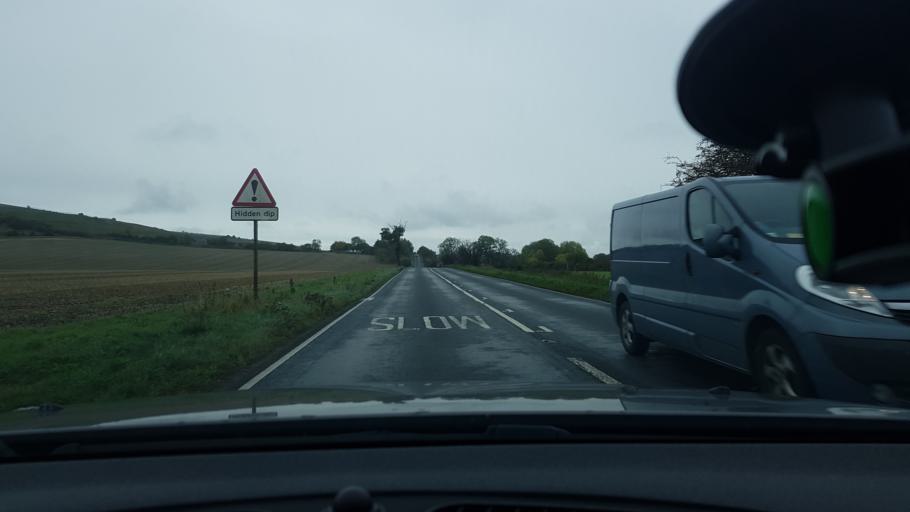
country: GB
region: England
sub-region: Borough of Swindon
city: Chiseldon
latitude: 51.4920
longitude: -1.7167
